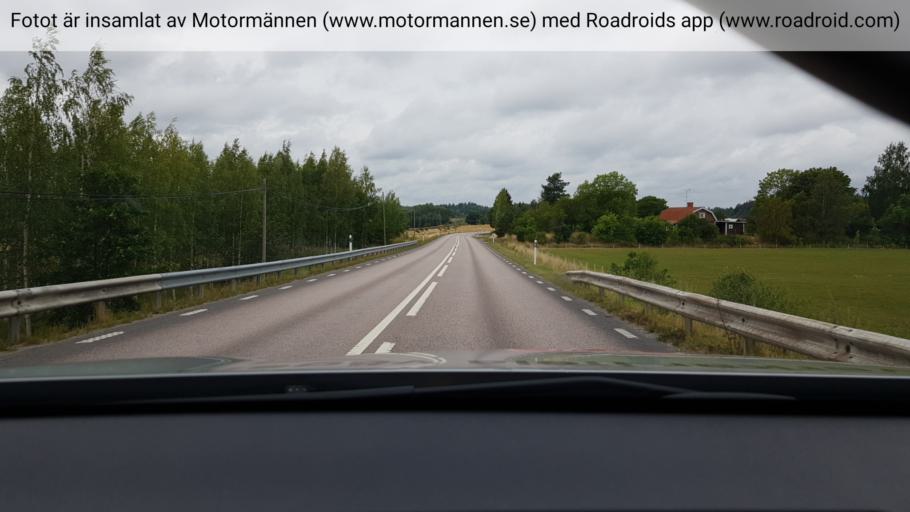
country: SE
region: Soedermanland
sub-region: Gnesta Kommun
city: Gnesta
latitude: 59.0581
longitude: 17.1901
